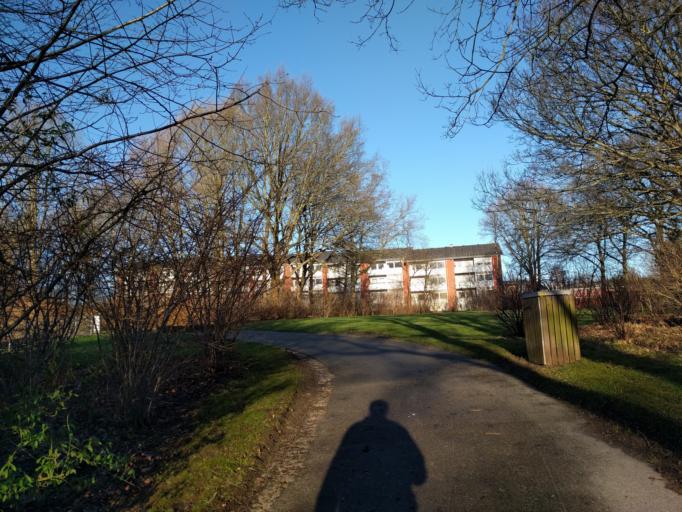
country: DK
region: Central Jutland
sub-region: Viborg Kommune
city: Viborg
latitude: 56.4637
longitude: 9.4153
